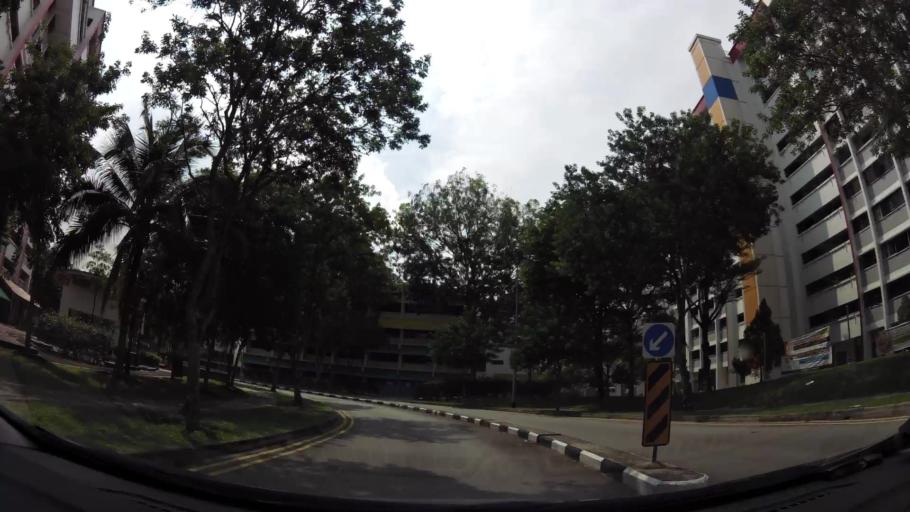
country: SG
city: Singapore
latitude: 1.3586
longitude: 103.9507
